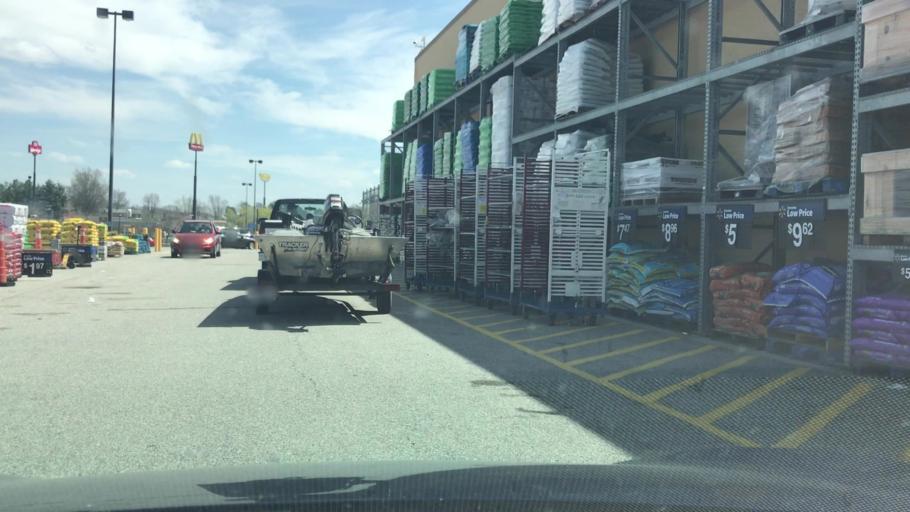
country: US
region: Virginia
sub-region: Pulaski County
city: Dublin
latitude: 37.0844
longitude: -80.6935
